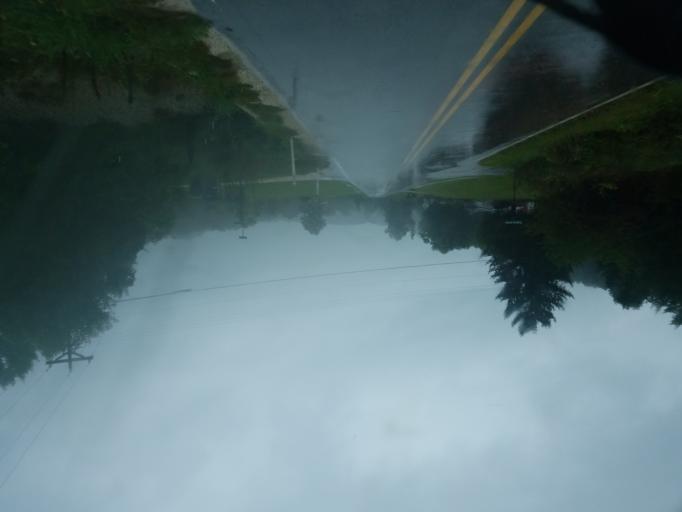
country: US
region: Kentucky
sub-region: Carter County
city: Grayson
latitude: 38.4746
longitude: -83.0342
